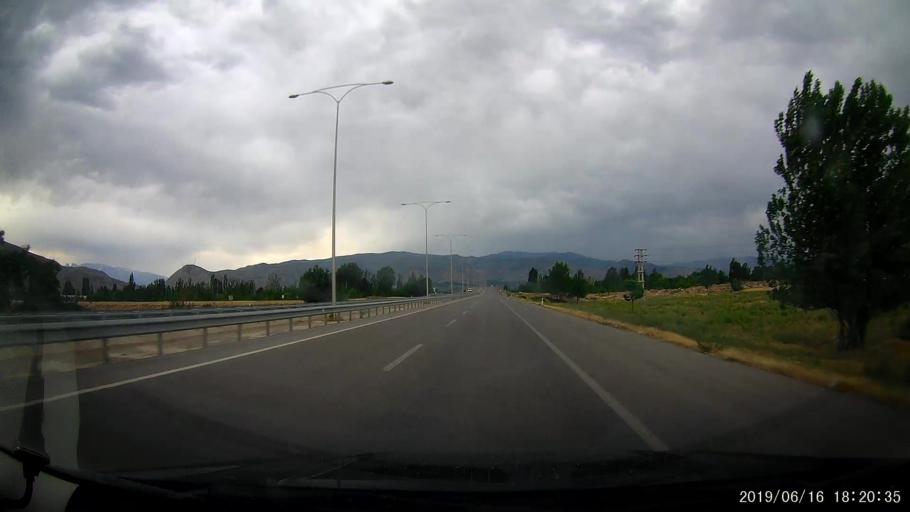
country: TR
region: Erzincan
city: Erzincan
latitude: 39.7200
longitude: 39.4658
